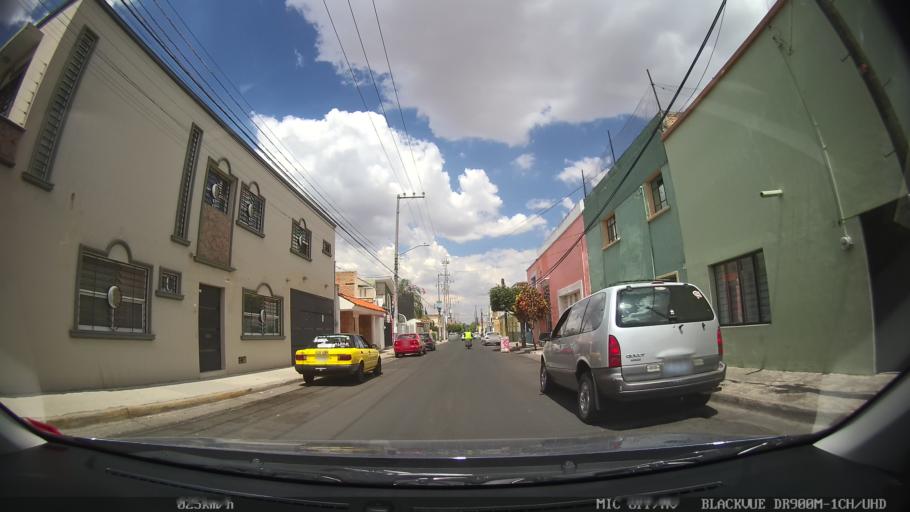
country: MX
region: Jalisco
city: Tlaquepaque
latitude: 20.6590
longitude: -103.2765
